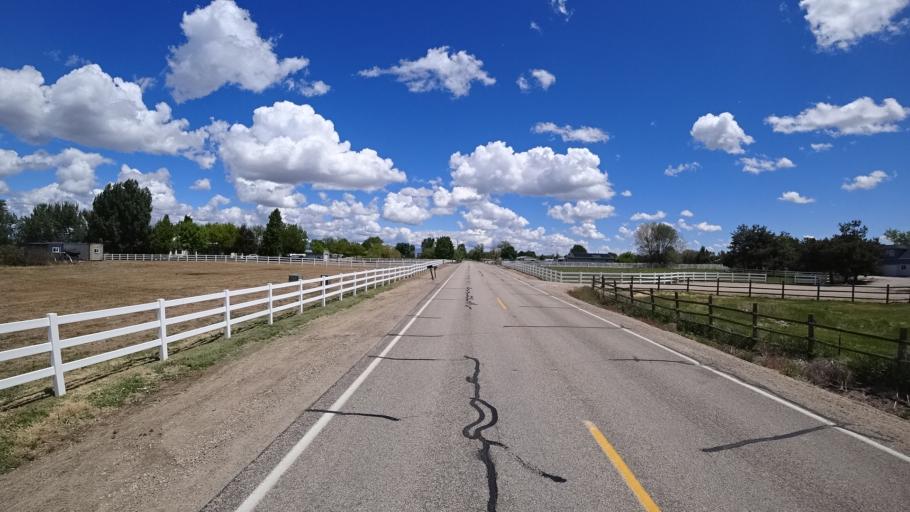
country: US
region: Idaho
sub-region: Ada County
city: Meridian
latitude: 43.5830
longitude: -116.4373
